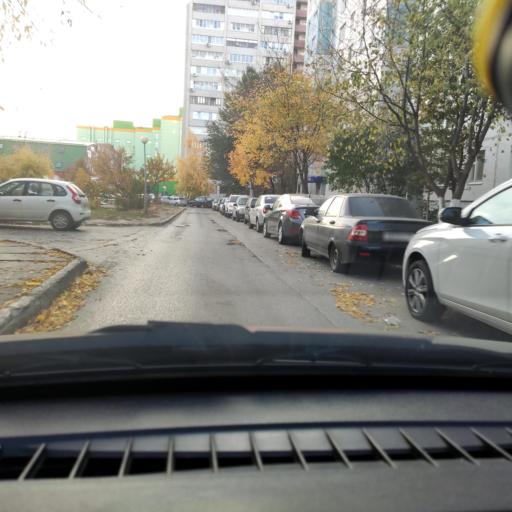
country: RU
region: Samara
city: Tol'yatti
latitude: 53.5443
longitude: 49.3571
